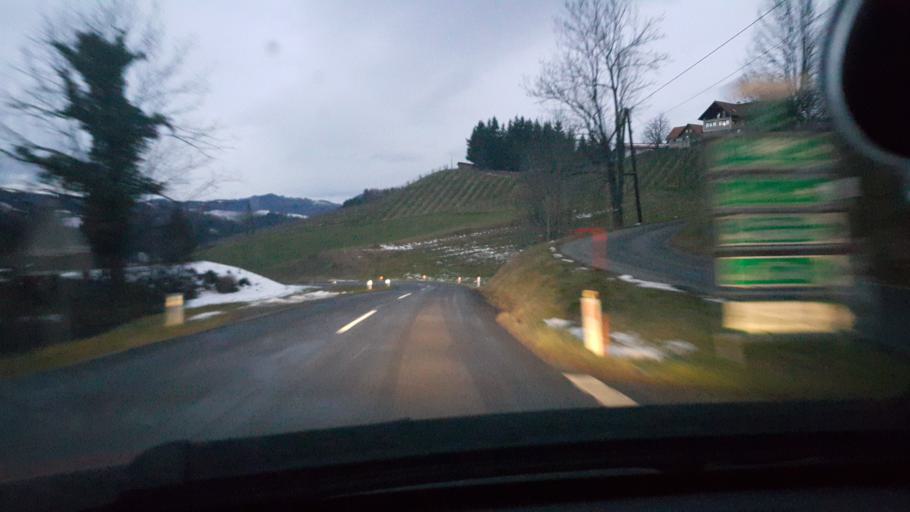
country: AT
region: Styria
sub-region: Politischer Bezirk Leibnitz
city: Leutschach
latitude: 46.6445
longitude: 15.5115
